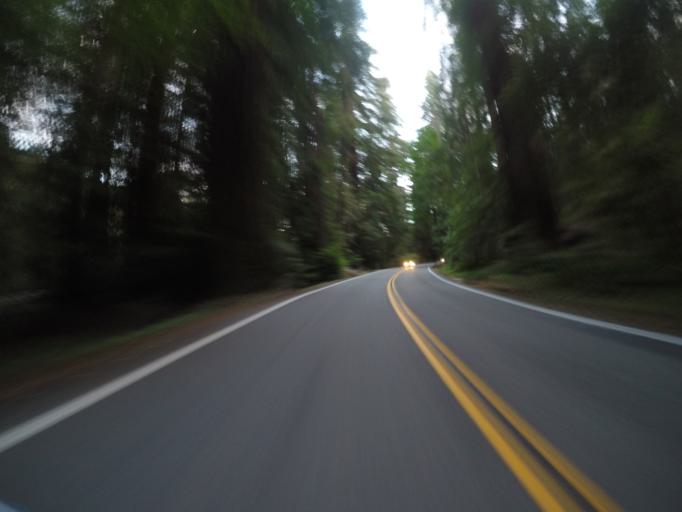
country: US
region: California
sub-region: Humboldt County
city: Redway
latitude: 40.0193
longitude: -123.7914
